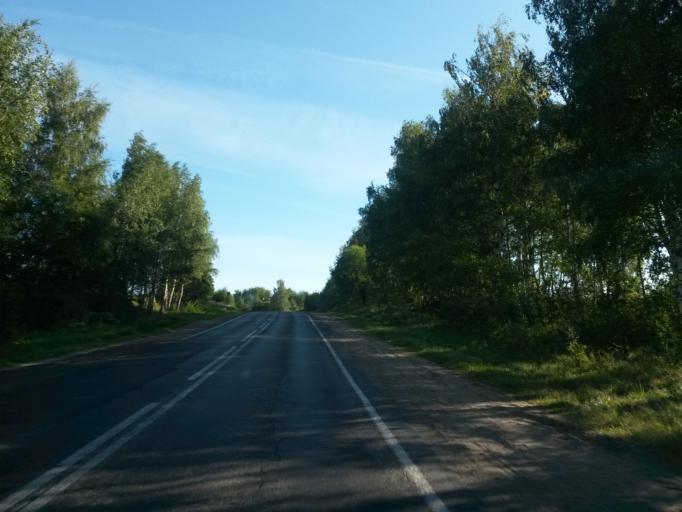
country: RU
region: Jaroslavl
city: Yaroslavl
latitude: 57.5461
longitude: 39.8617
